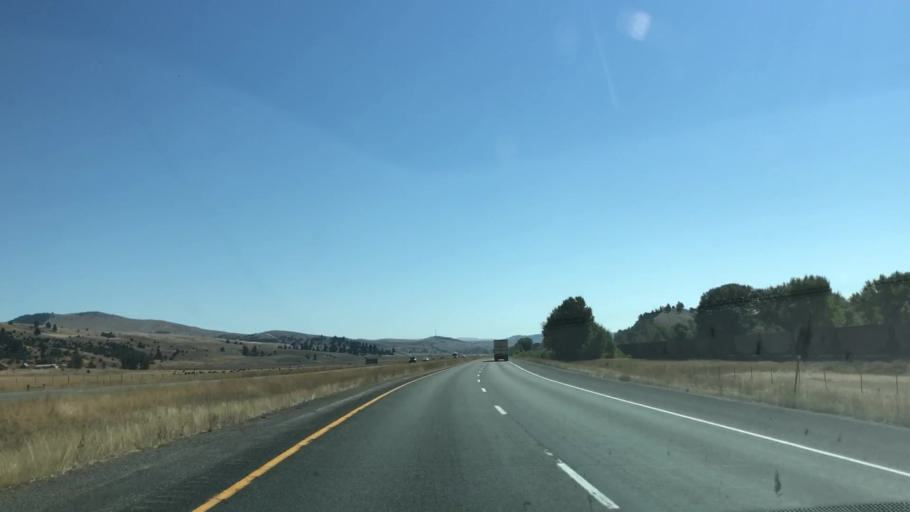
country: US
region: Montana
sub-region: Powell County
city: Deer Lodge
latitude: 46.6066
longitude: -112.9811
